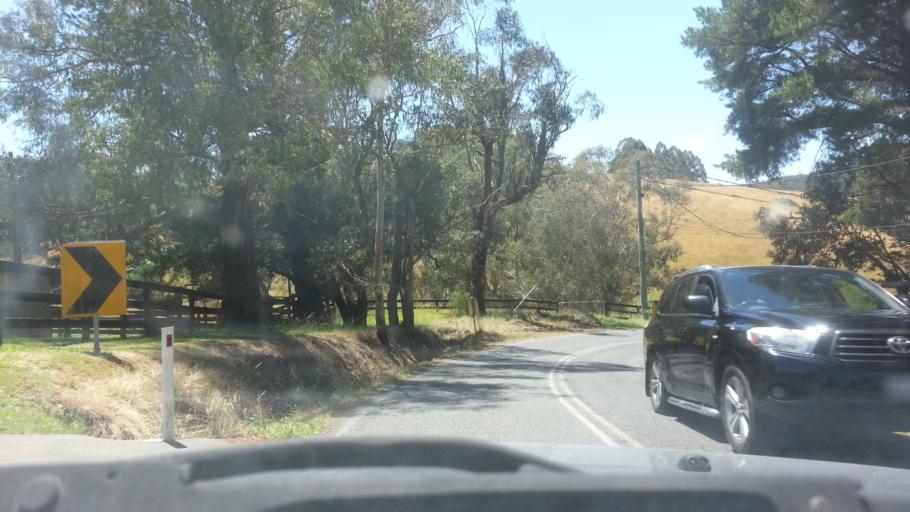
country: AU
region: Victoria
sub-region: Cardinia
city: Beaconsfield Upper
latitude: -37.9732
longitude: 145.3780
